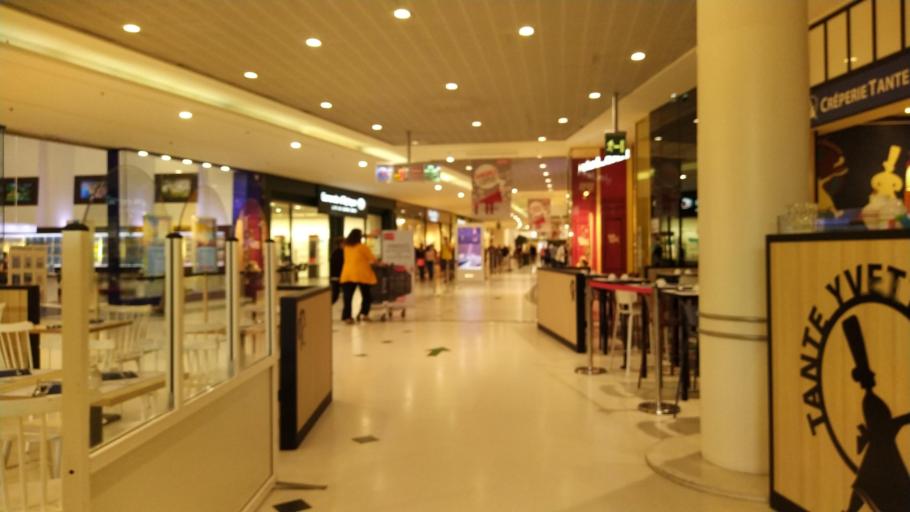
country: FR
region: Pays de la Loire
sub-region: Departement de la Loire-Atlantique
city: Sainte-Luce-sur-Loire
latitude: 47.2484
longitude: -1.5136
